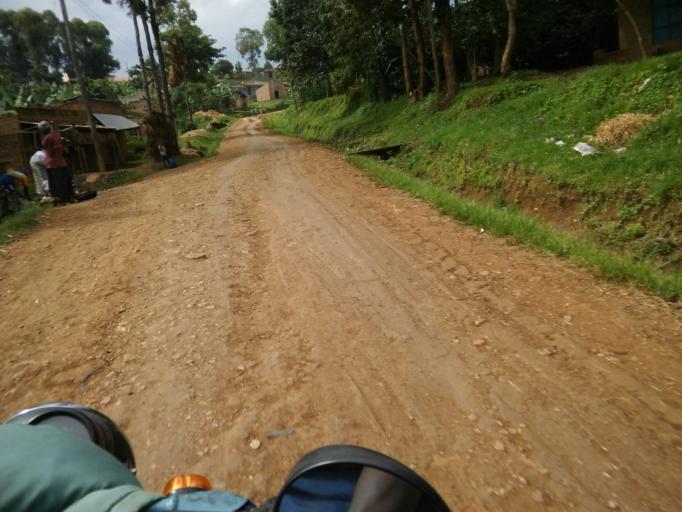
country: UG
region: Eastern Region
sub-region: Manafwa District
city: Manafwa
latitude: 0.9043
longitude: 34.3562
